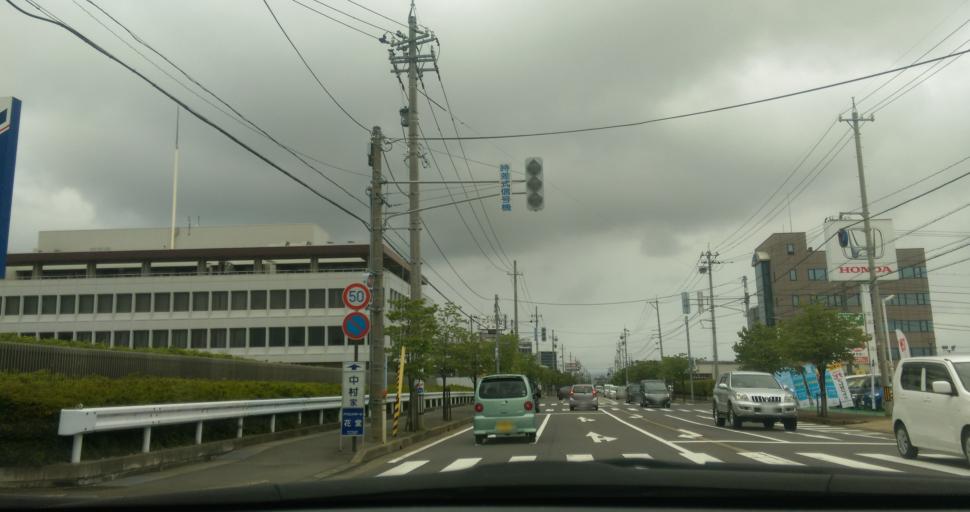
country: JP
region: Fukui
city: Fukui-shi
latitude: 36.0216
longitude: 136.2082
